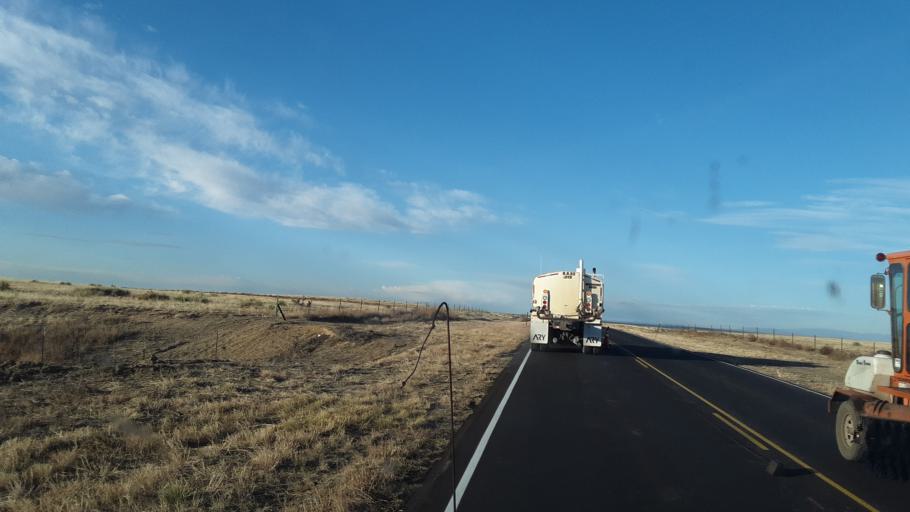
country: US
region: Colorado
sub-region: Otero County
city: Rocky Ford
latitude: 37.9614
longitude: -103.8466
